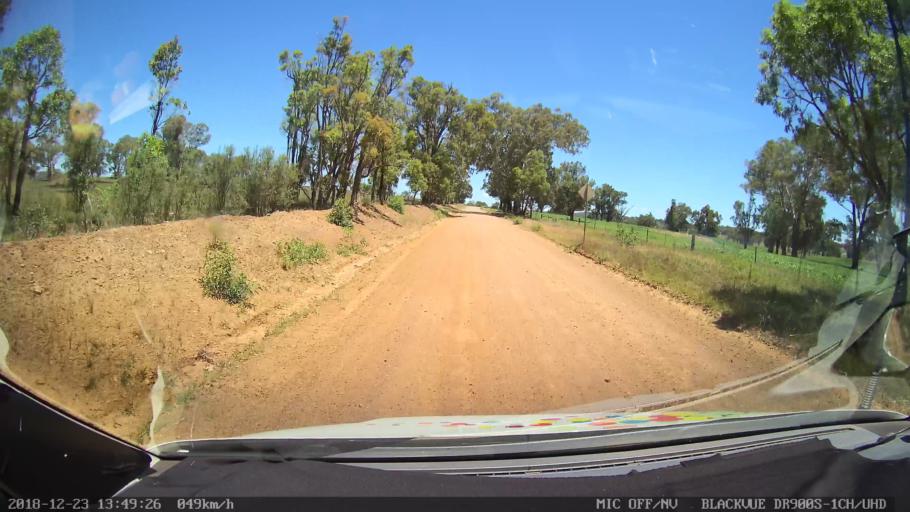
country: AU
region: New South Wales
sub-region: Tamworth Municipality
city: Manilla
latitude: -30.5213
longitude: 151.1083
